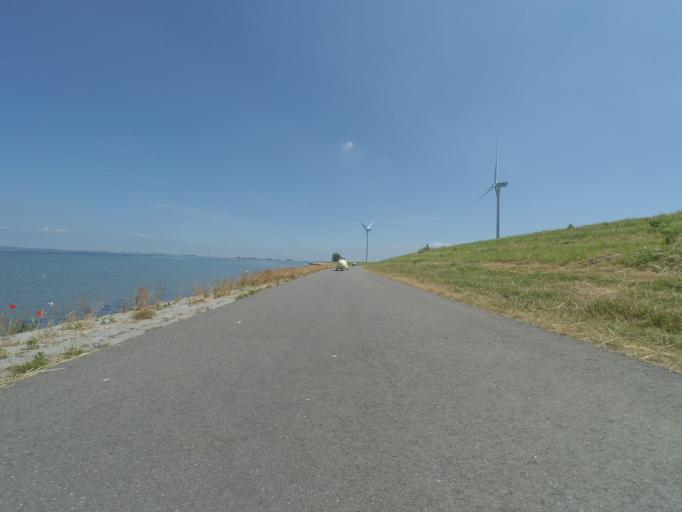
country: NL
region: Zeeland
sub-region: Schouwen-Duiveland
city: Bruinisse
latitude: 51.6118
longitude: 4.0661
